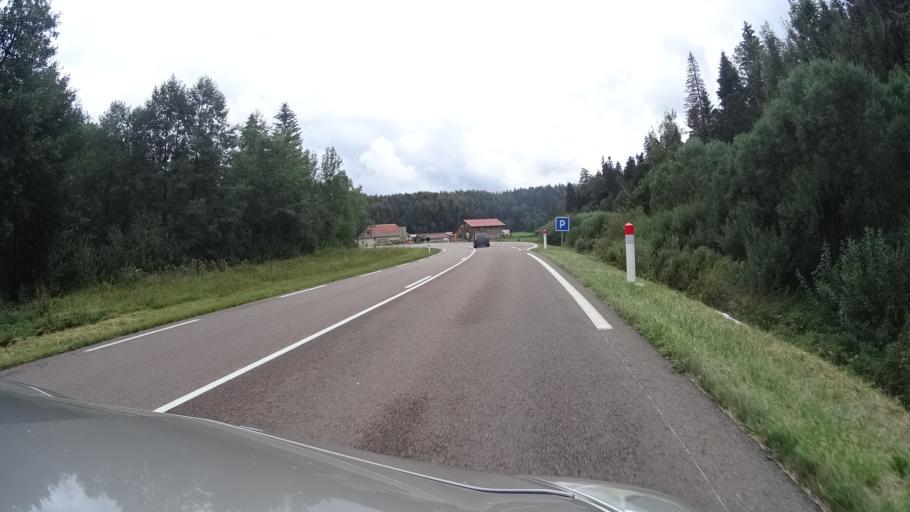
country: FR
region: Franche-Comte
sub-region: Departement du Jura
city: Champagnole
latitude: 46.6431
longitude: 5.9399
